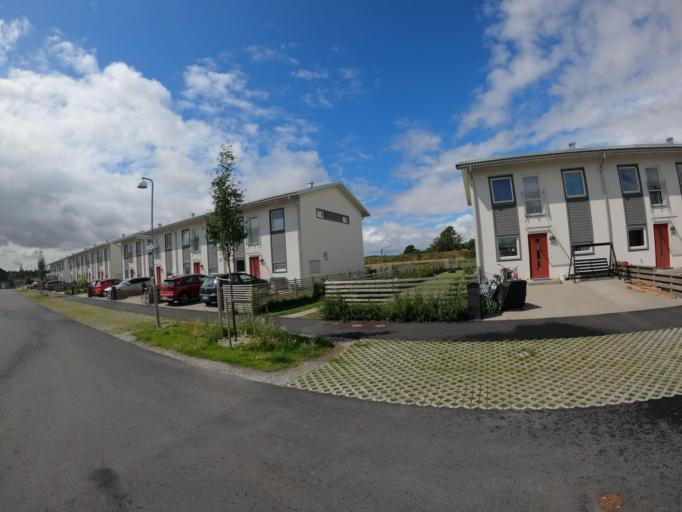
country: SE
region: Skane
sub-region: Eslovs Kommun
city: Eslov
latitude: 55.7257
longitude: 13.3587
